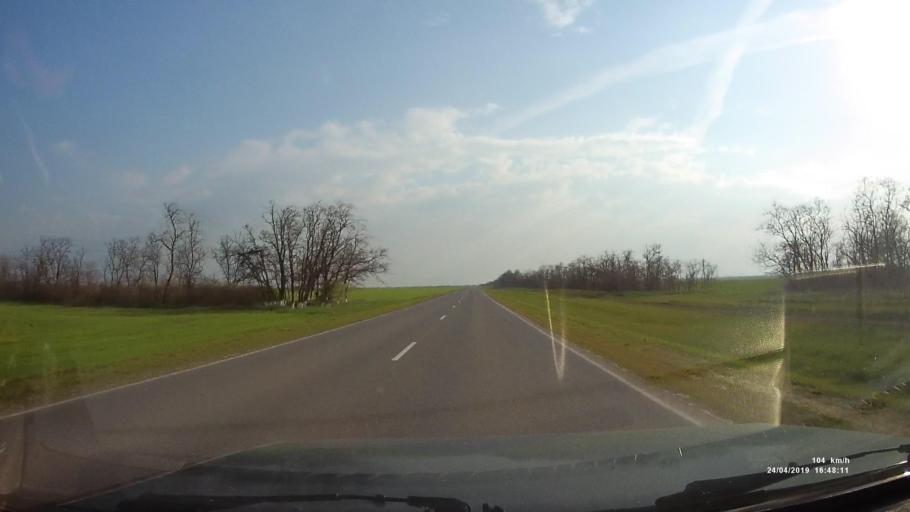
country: RU
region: Rostov
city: Proletarsk
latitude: 46.7343
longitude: 41.7779
